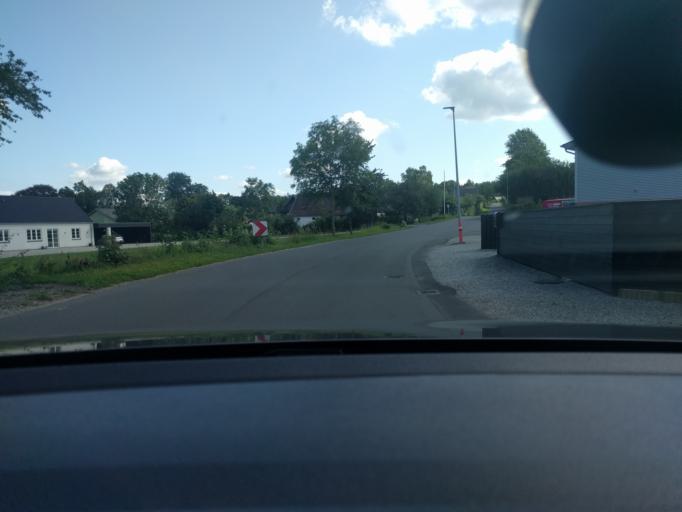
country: DK
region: Central Jutland
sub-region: Viborg Kommune
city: Viborg
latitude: 56.5251
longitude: 9.3674
